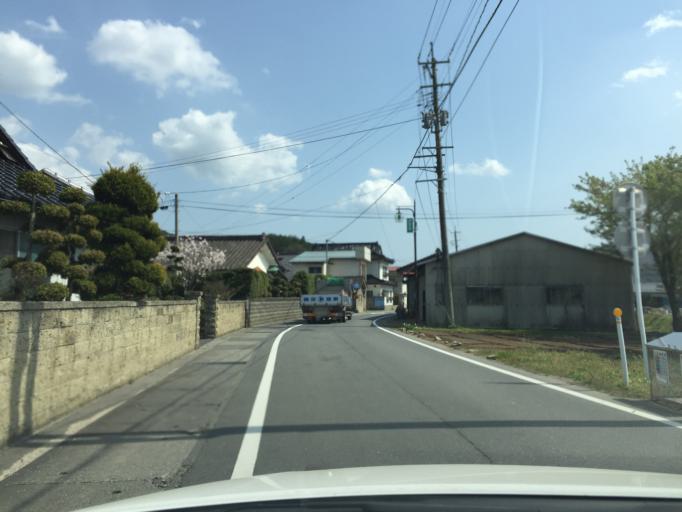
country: JP
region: Fukushima
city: Namie
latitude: 37.3462
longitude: 140.8036
